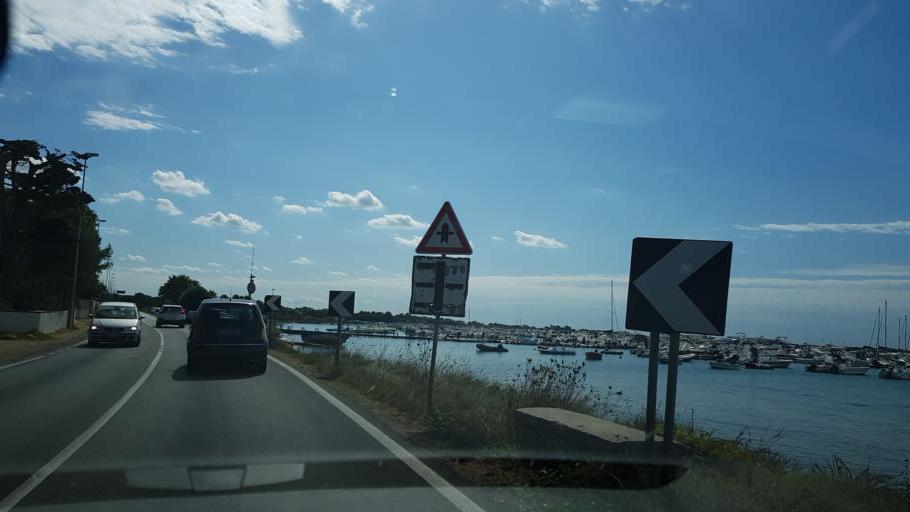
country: IT
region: Apulia
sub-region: Provincia di Lecce
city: Porto Cesareo
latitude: 40.2548
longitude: 17.9057
